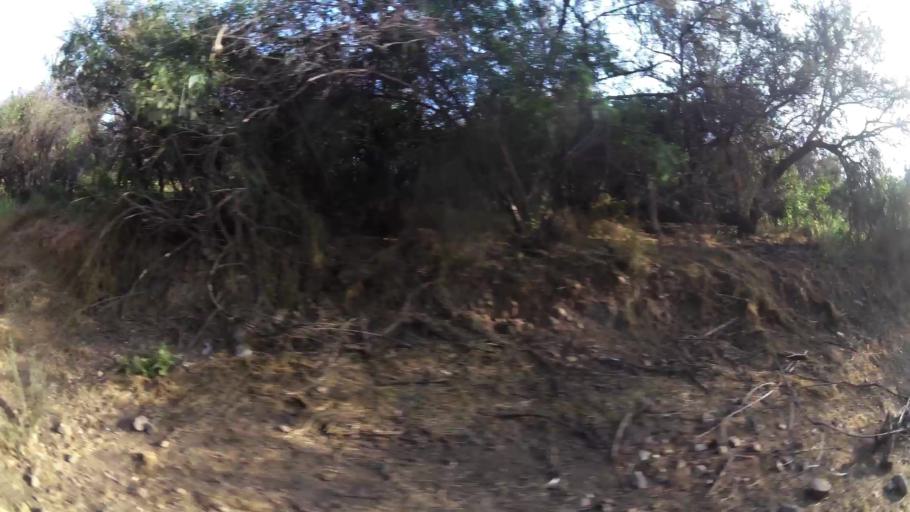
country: CL
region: Santiago Metropolitan
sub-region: Provincia de Santiago
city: Villa Presidente Frei, Nunoa, Santiago, Chile
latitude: -33.3920
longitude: -70.5351
